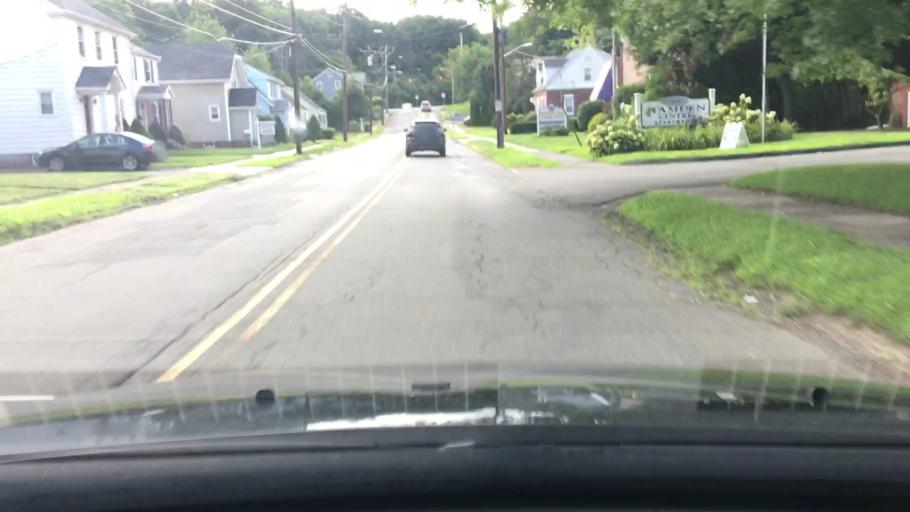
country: US
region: Connecticut
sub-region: New Haven County
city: Hamden
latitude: 41.3850
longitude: -72.9048
